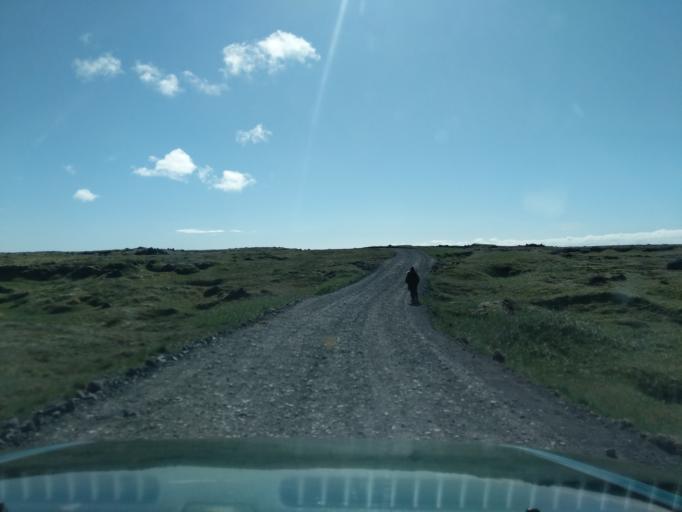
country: IS
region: West
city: Olafsvik
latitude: 64.8749
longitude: -24.0011
